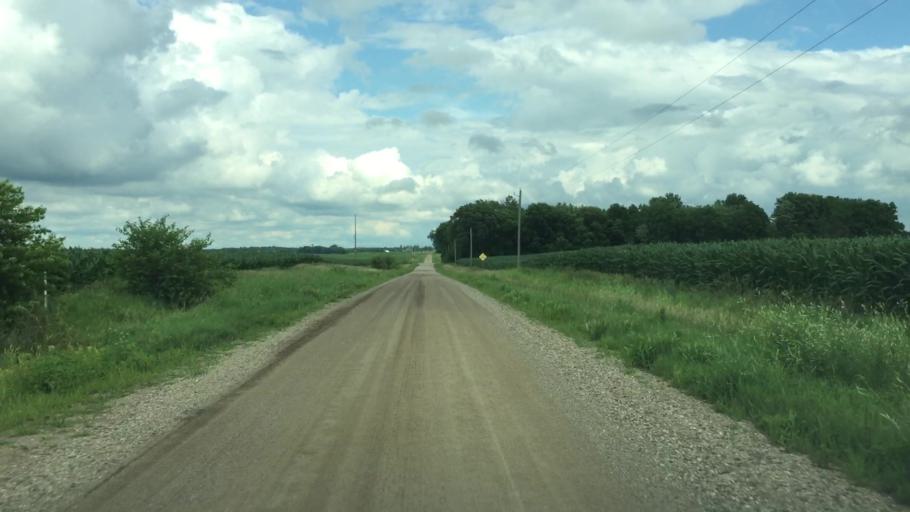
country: US
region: Iowa
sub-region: Jasper County
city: Newton
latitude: 41.7459
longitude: -93.0244
